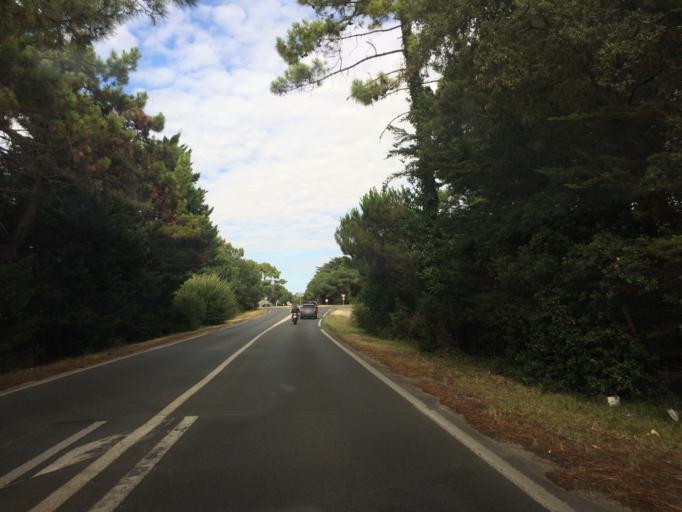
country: FR
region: Poitou-Charentes
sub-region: Departement de la Charente-Maritime
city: La Flotte
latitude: 46.1793
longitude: -1.3260
